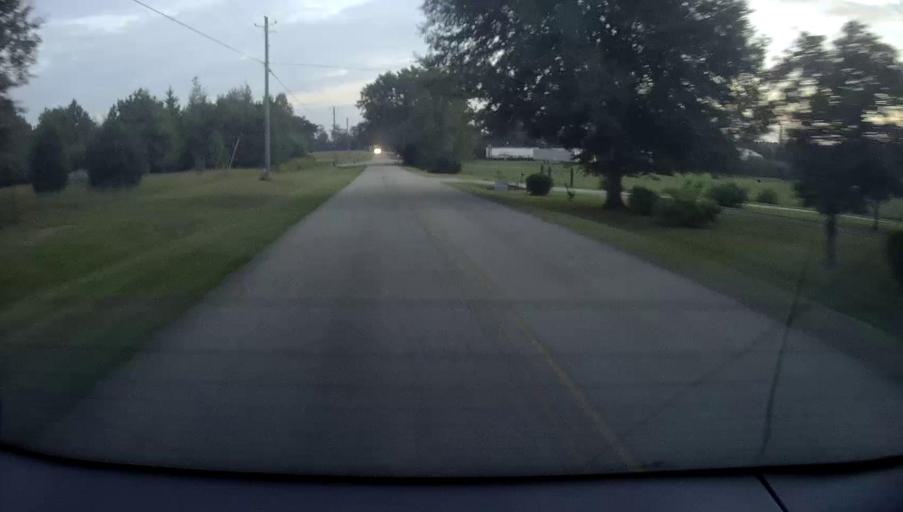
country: US
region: Georgia
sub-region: Henry County
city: Locust Grove
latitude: 33.3275
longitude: -84.0427
